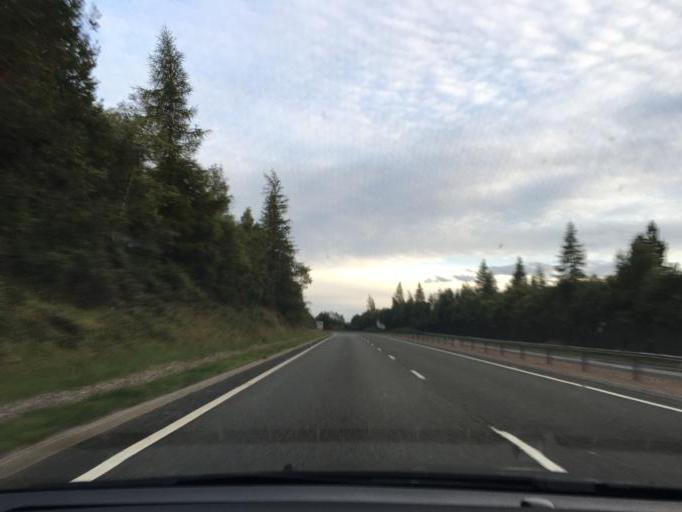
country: GB
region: Scotland
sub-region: Highland
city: Aviemore
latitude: 57.3270
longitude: -3.9780
